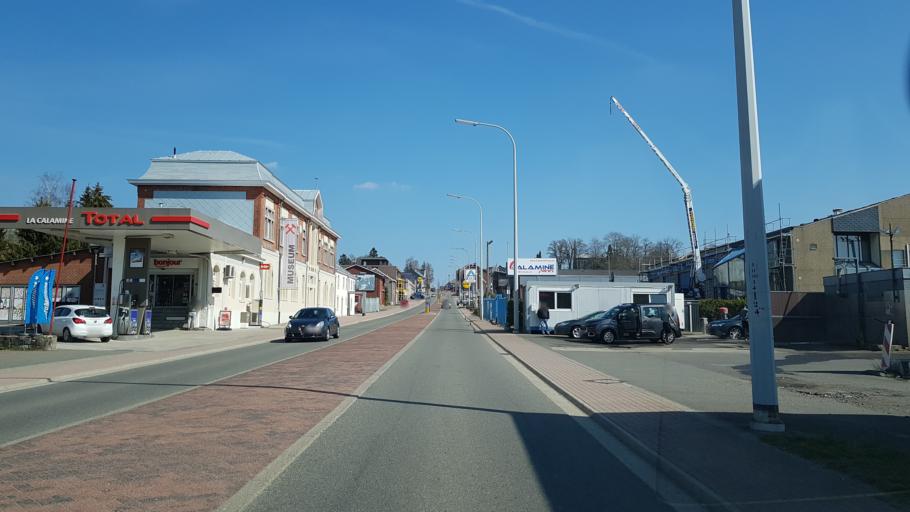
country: BE
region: Wallonia
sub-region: Province de Liege
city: La Calamine
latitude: 50.7109
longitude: 6.0080
